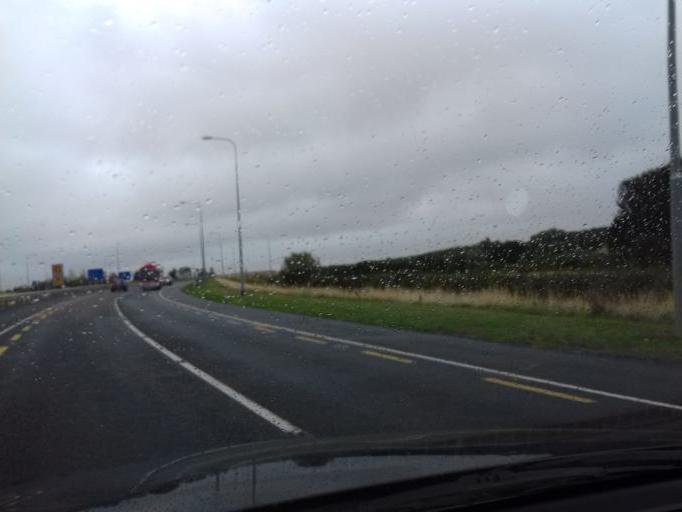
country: IE
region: Leinster
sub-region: County Carlow
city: Bagenalstown
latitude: 52.7678
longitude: -6.9549
